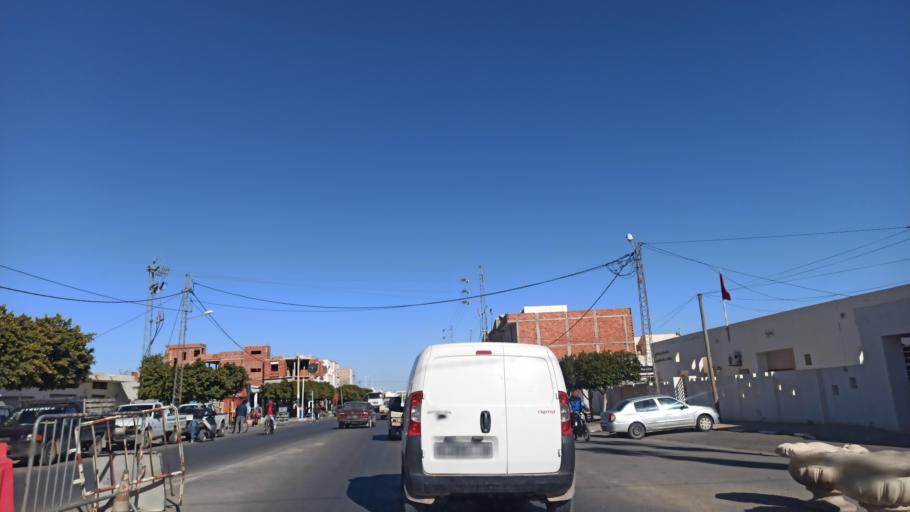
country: TN
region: Sidi Bu Zayd
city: Bi'r al Hufayy
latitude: 34.9271
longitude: 9.1920
